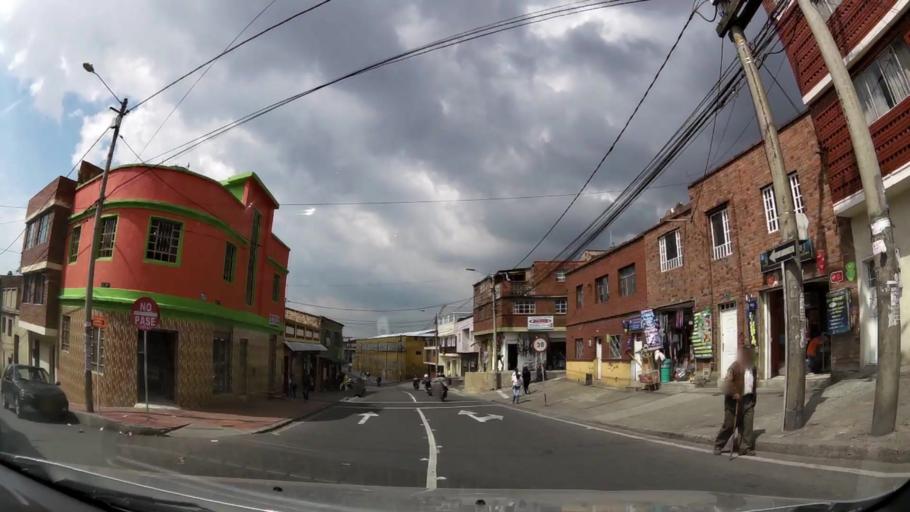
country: CO
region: Bogota D.C.
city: Bogota
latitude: 4.5660
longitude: -74.0941
